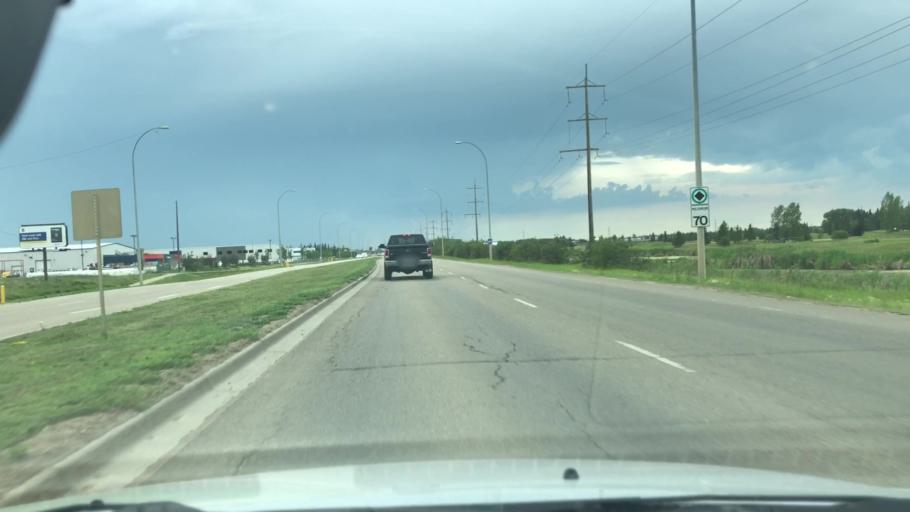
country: CA
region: Alberta
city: St. Albert
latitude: 53.5995
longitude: -113.5920
